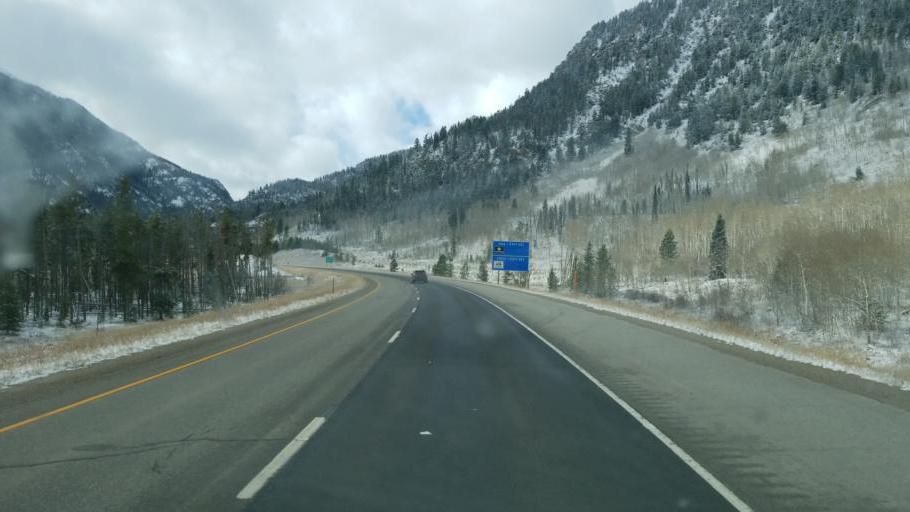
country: US
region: Colorado
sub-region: Summit County
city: Frisco
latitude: 39.5865
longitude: -106.1076
